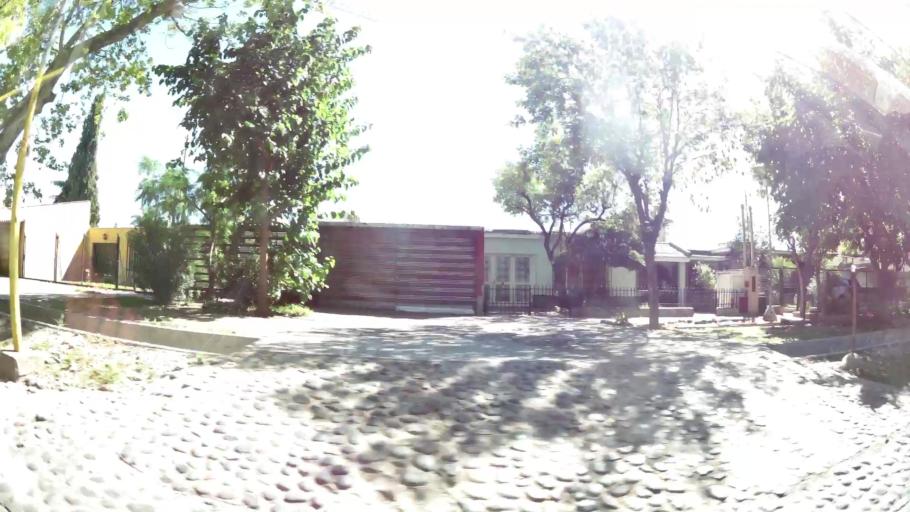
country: AR
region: Mendoza
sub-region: Departamento de Godoy Cruz
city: Godoy Cruz
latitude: -32.9452
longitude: -68.8095
